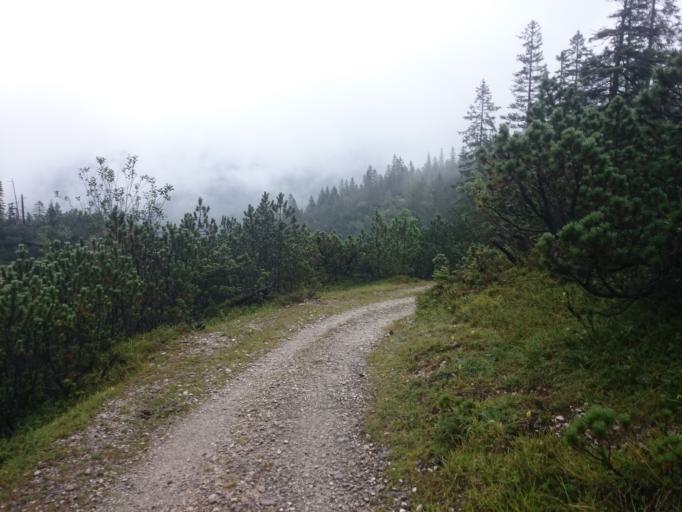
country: AT
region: Tyrol
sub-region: Politischer Bezirk Innsbruck Land
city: Thaur
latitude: 47.4152
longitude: 11.4706
